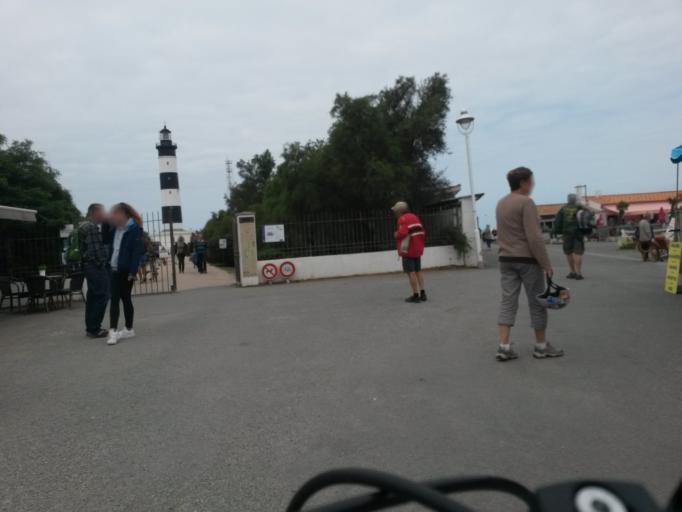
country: FR
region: Poitou-Charentes
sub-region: Departement de la Charente-Maritime
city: Saint-Denis-d'Oleron
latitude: 46.0462
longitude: -1.4076
